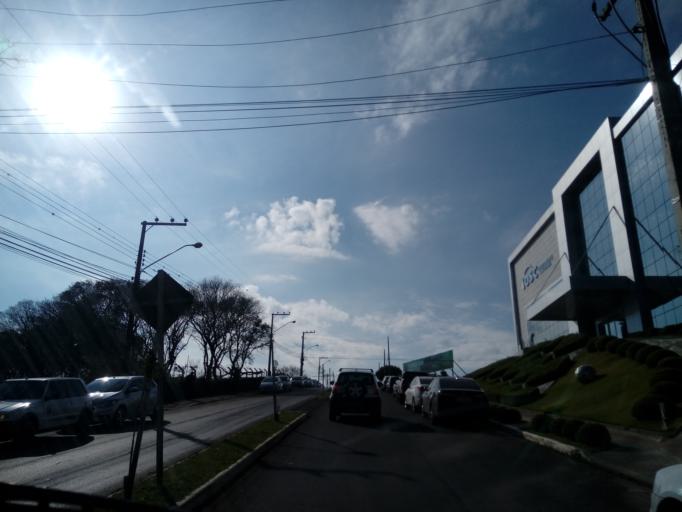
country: BR
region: Santa Catarina
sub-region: Chapeco
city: Chapeco
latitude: -27.1095
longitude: -52.5986
